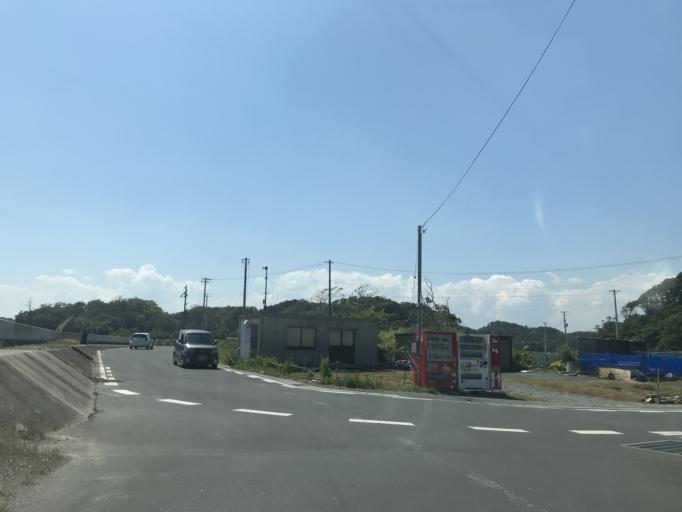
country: JP
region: Miyagi
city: Yamoto
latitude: 38.3285
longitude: 141.1650
